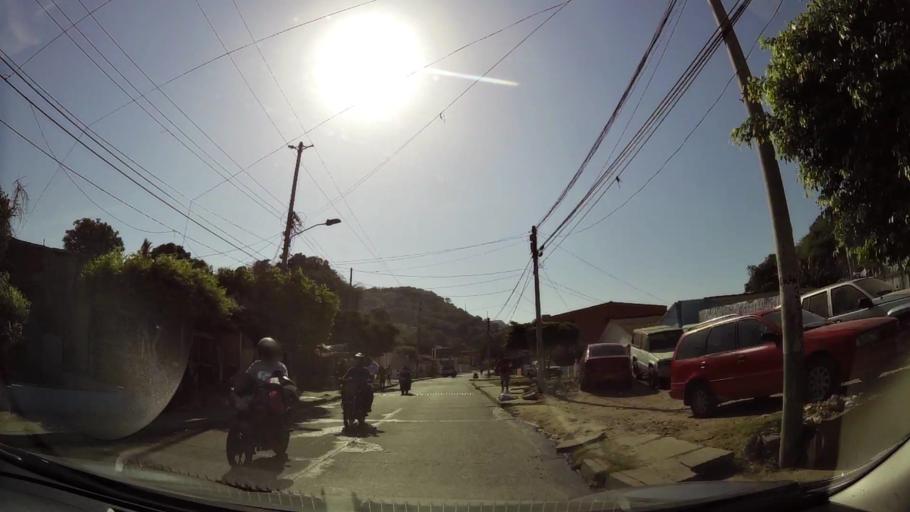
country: CO
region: Bolivar
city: Cartagena
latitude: 10.4282
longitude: -75.5330
